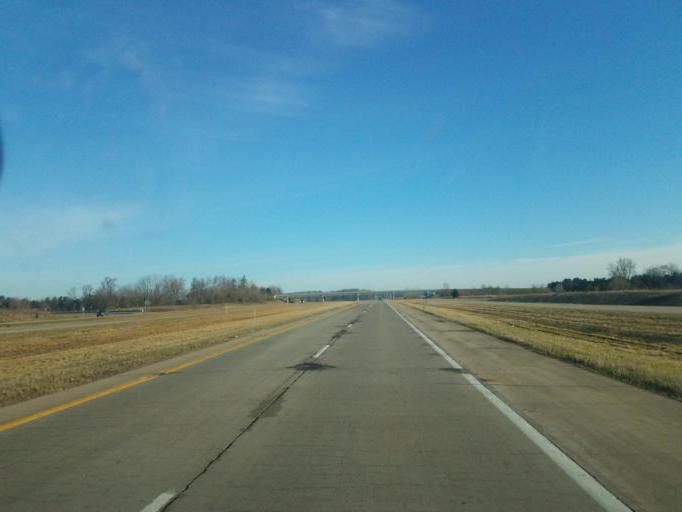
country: US
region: Michigan
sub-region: Clinton County
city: Bath
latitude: 42.8085
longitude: -84.5114
